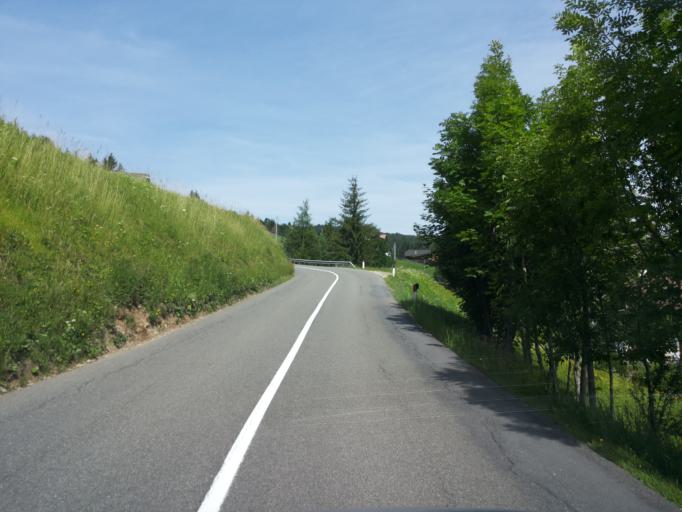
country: IT
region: Trentino-Alto Adige
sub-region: Bolzano
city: Ortisei
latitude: 46.5716
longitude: 11.6395
